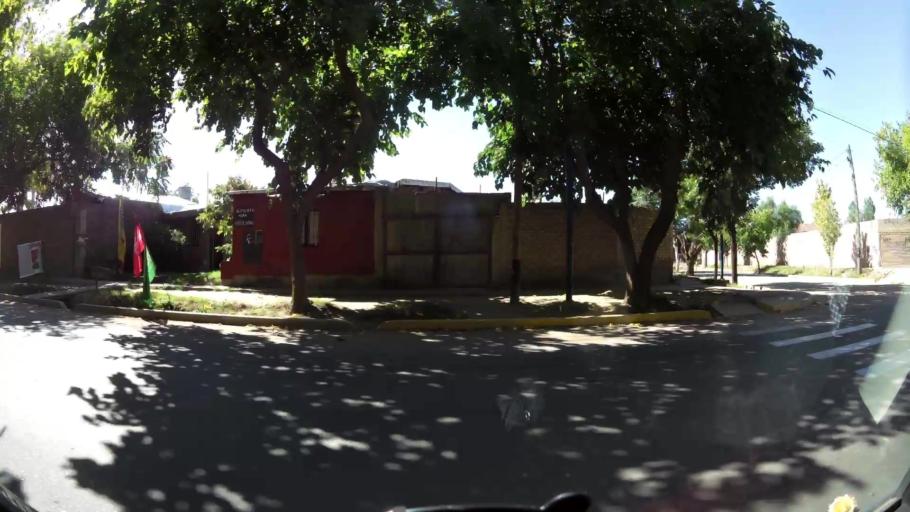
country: AR
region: Mendoza
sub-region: Departamento de Godoy Cruz
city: Godoy Cruz
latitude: -32.9539
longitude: -68.8239
